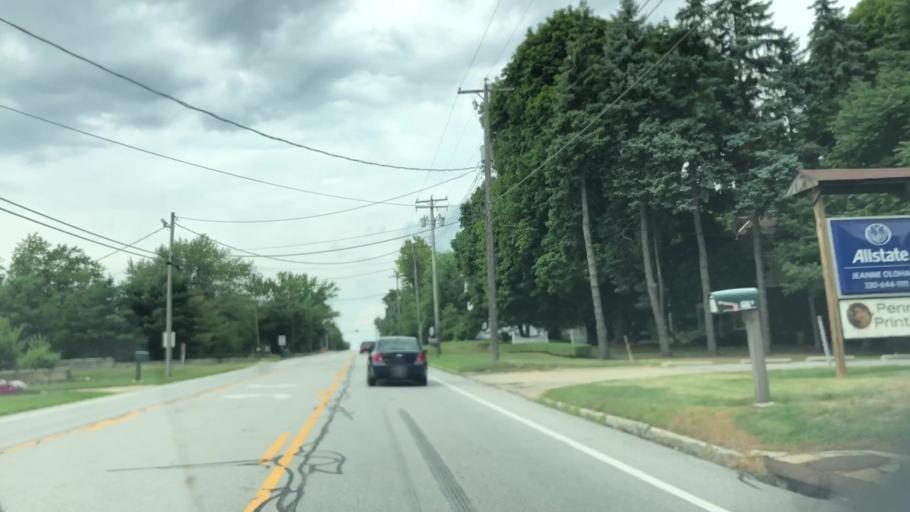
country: US
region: Ohio
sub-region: Summit County
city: Portage Lakes
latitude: 41.0066
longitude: -81.5238
